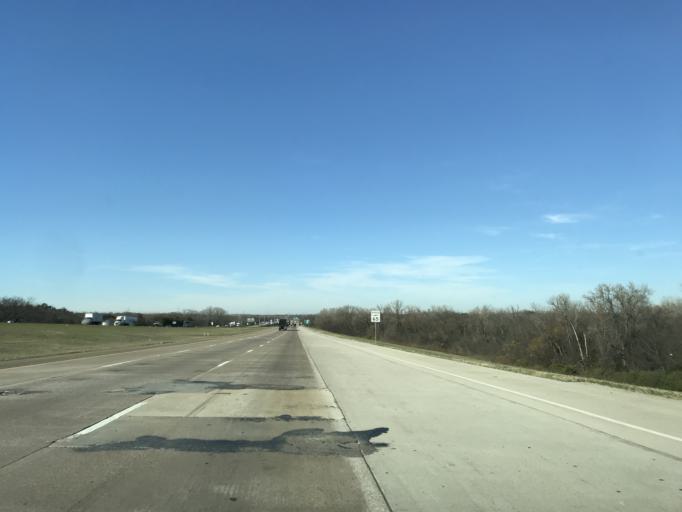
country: US
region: Texas
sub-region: Dallas County
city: Hutchins
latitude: 32.6713
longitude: -96.7347
